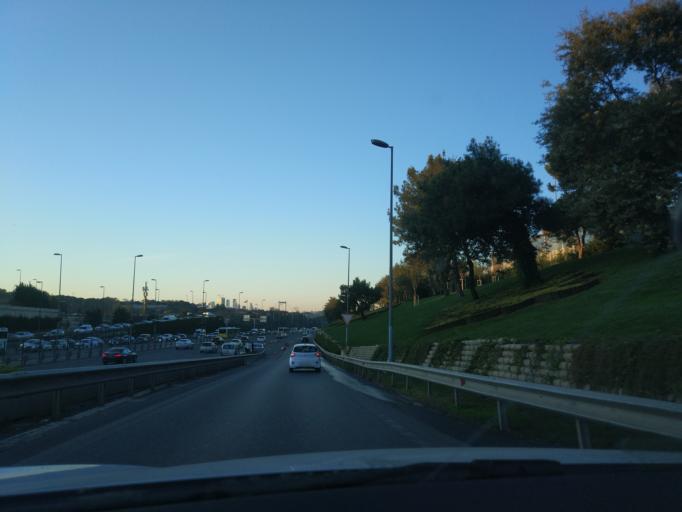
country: TR
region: Istanbul
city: UEskuedar
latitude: 41.0246
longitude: 29.0472
